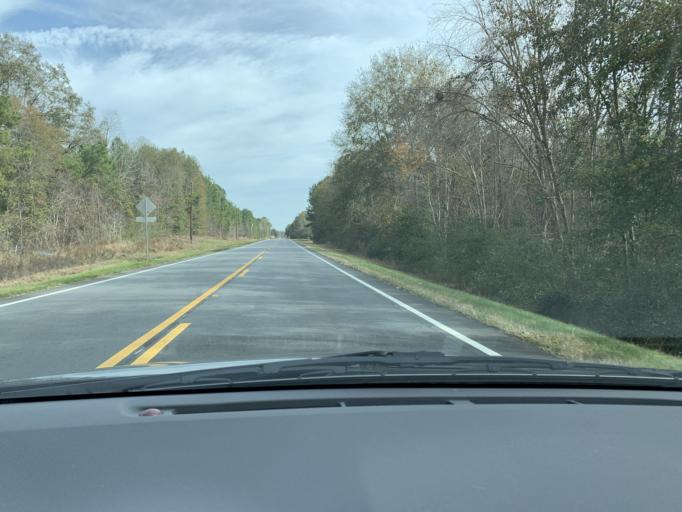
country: US
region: Georgia
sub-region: Wilcox County
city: Rochelle
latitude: 31.9585
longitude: -83.6084
